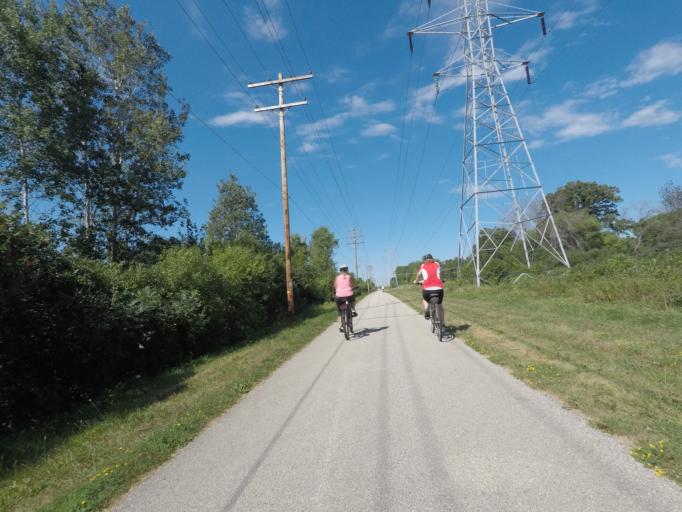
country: US
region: Wisconsin
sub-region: Waukesha County
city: Waukesha
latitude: 43.0099
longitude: -88.1840
